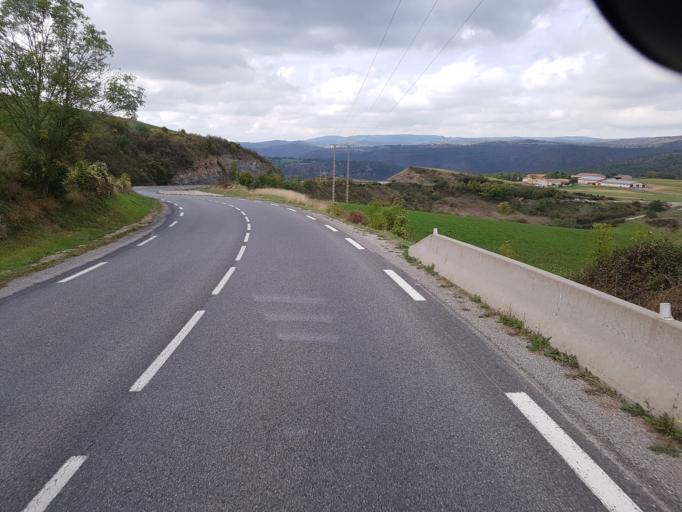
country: FR
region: Midi-Pyrenees
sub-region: Departement de l'Aveyron
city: Saint-Georges-de-Luzencon
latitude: 44.0791
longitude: 3.0089
